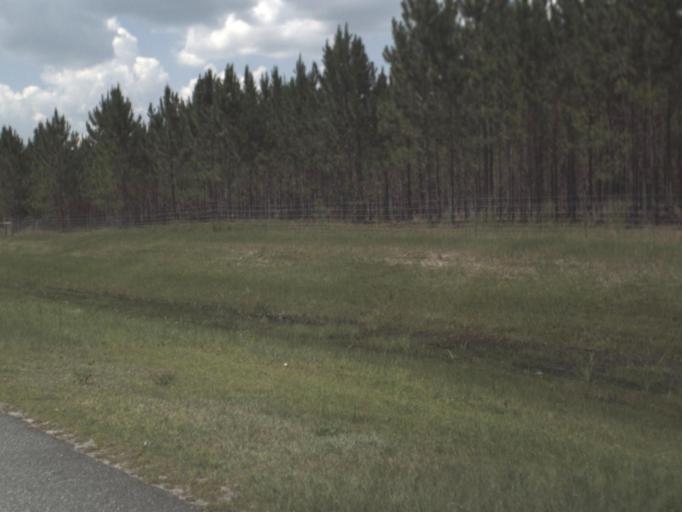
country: US
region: Florida
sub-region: Bradford County
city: Starke
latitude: 30.0022
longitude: -82.0517
